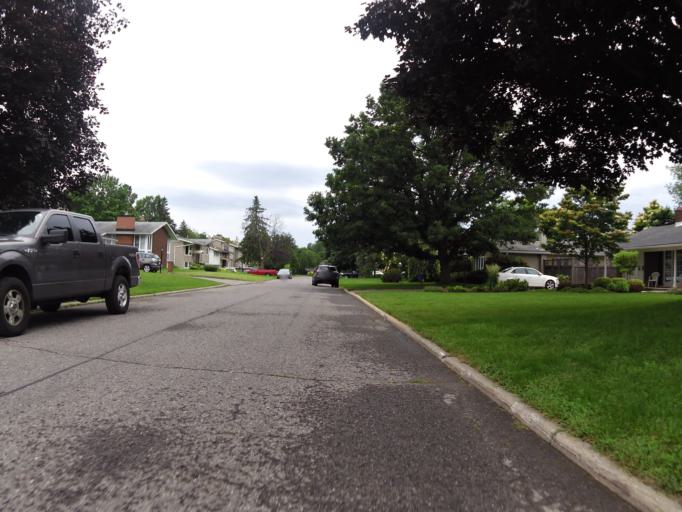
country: CA
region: Ontario
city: Bells Corners
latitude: 45.3382
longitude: -75.7890
